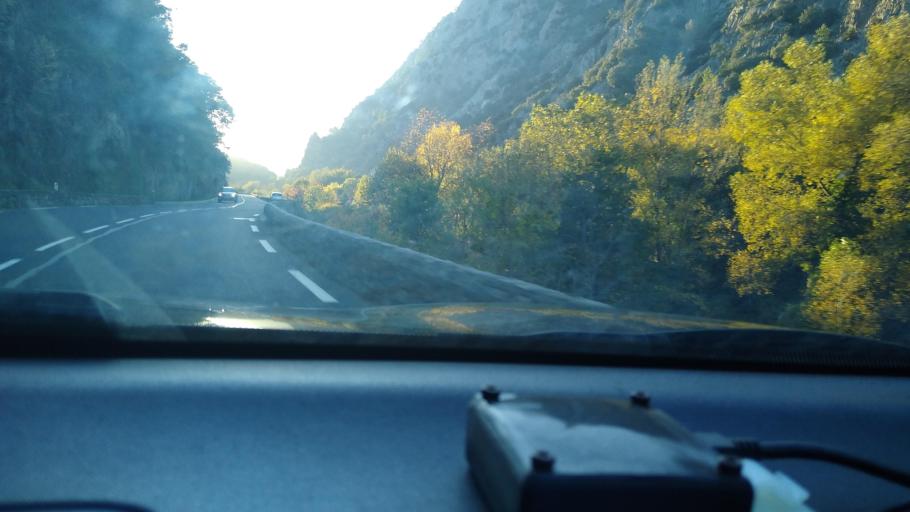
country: FR
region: Languedoc-Roussillon
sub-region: Departement des Pyrenees-Orientales
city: Vernet-les-Bains
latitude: 42.5276
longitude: 2.2418
